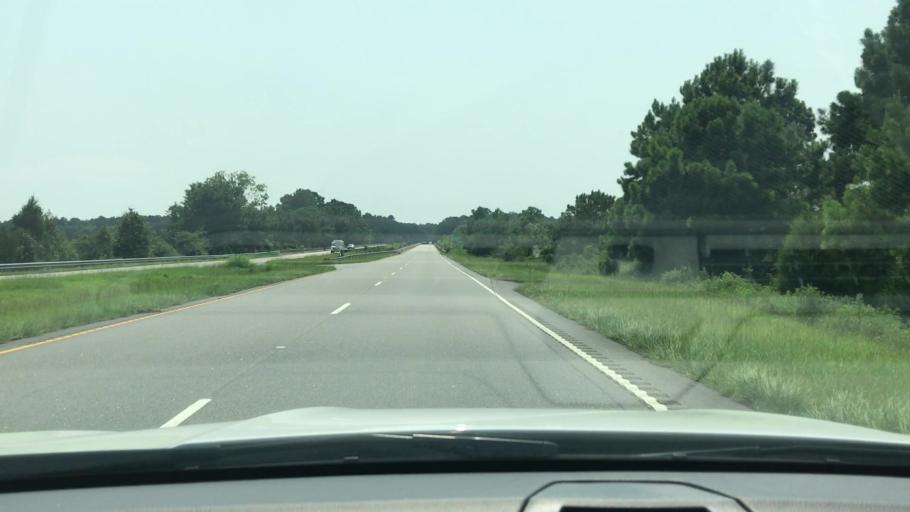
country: US
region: South Carolina
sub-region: Georgetown County
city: Georgetown
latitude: 33.1887
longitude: -79.4019
